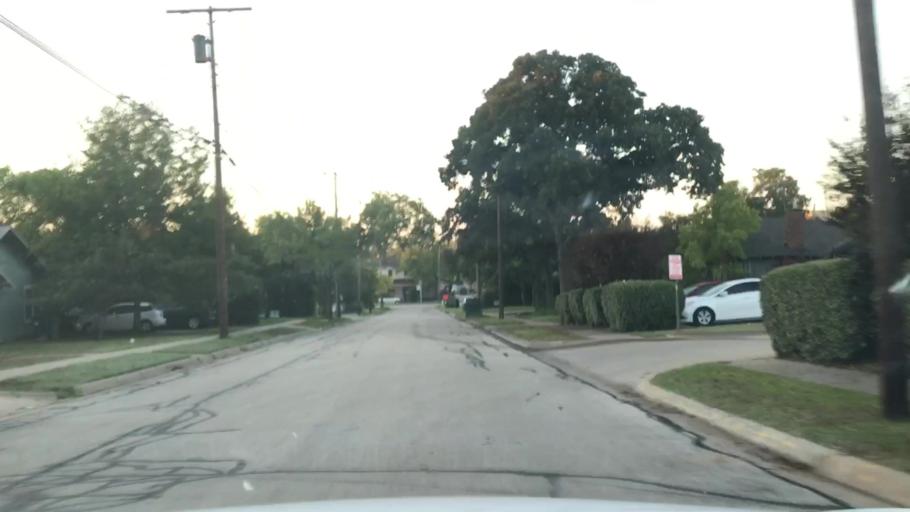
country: US
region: Texas
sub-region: Denton County
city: Denton
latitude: 33.2173
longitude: -97.1479
